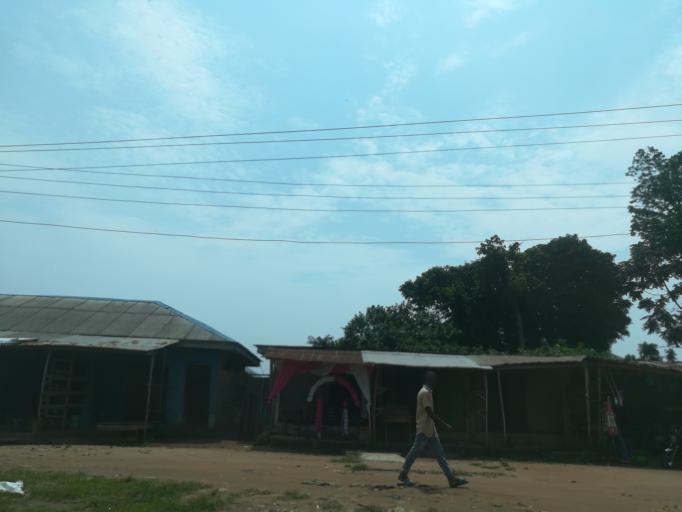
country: NG
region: Lagos
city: Ikorodu
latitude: 6.5852
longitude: 3.6253
